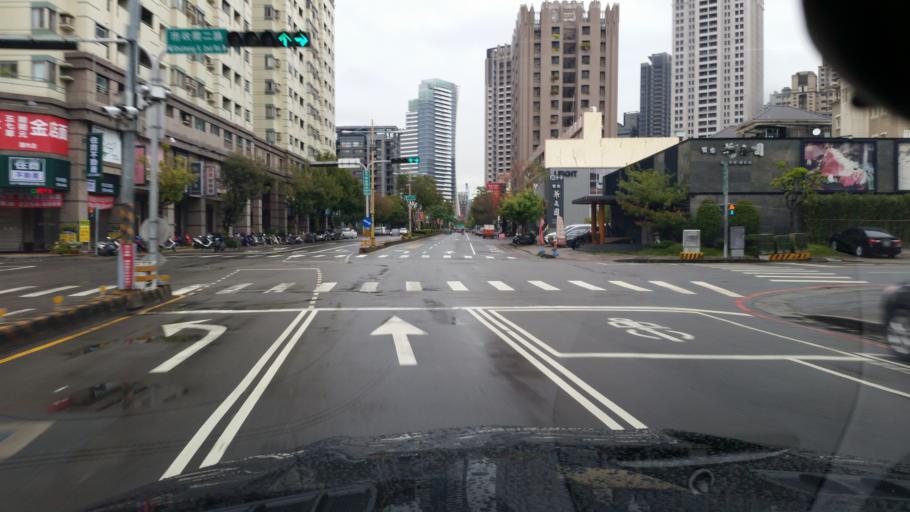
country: TW
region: Taiwan
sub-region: Taichung City
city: Taichung
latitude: 24.1556
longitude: 120.6365
